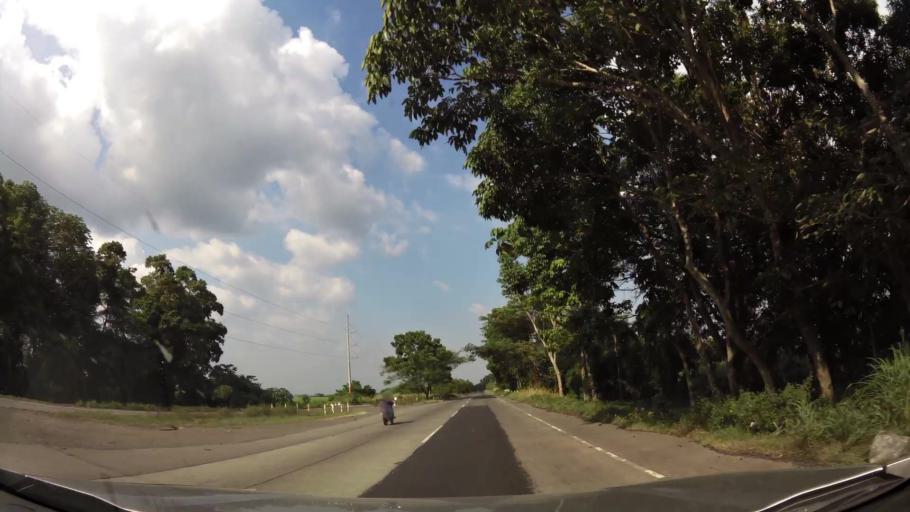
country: GT
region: Escuintla
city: Puerto San Jose
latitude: 14.0447
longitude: -90.7779
